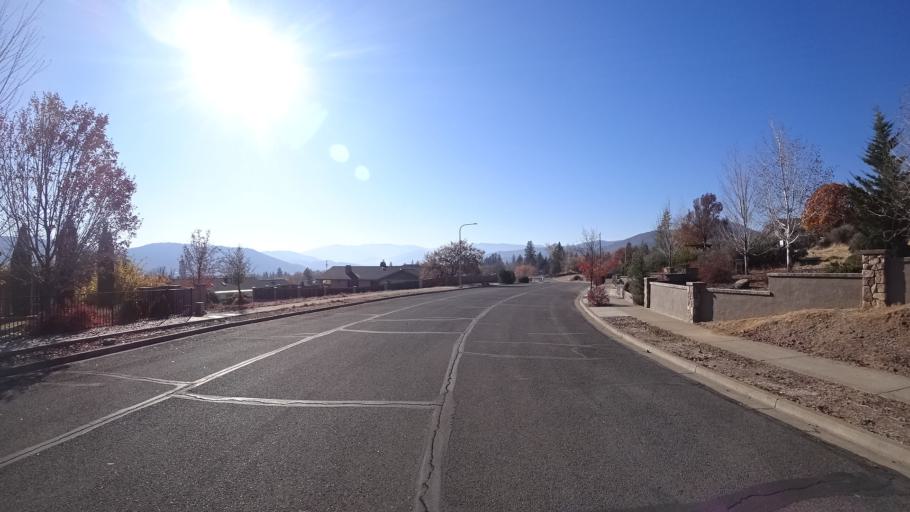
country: US
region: California
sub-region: Siskiyou County
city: Yreka
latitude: 41.7439
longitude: -122.6440
